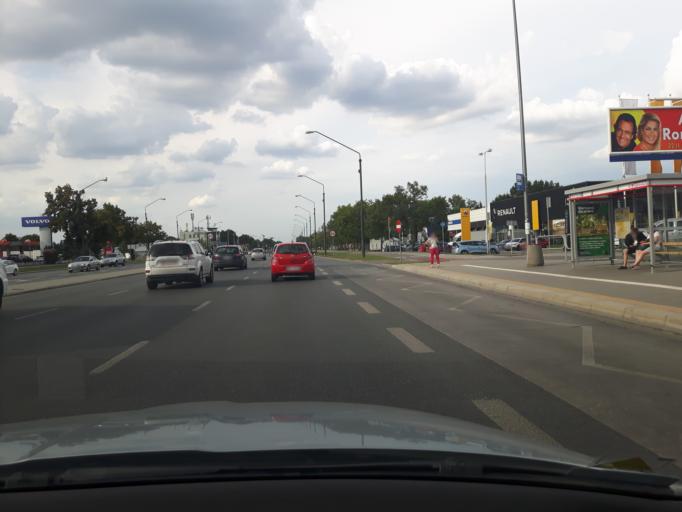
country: PL
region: Masovian Voivodeship
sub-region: Powiat piaseczynski
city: Mysiadlo
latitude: 52.1064
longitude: 21.0188
